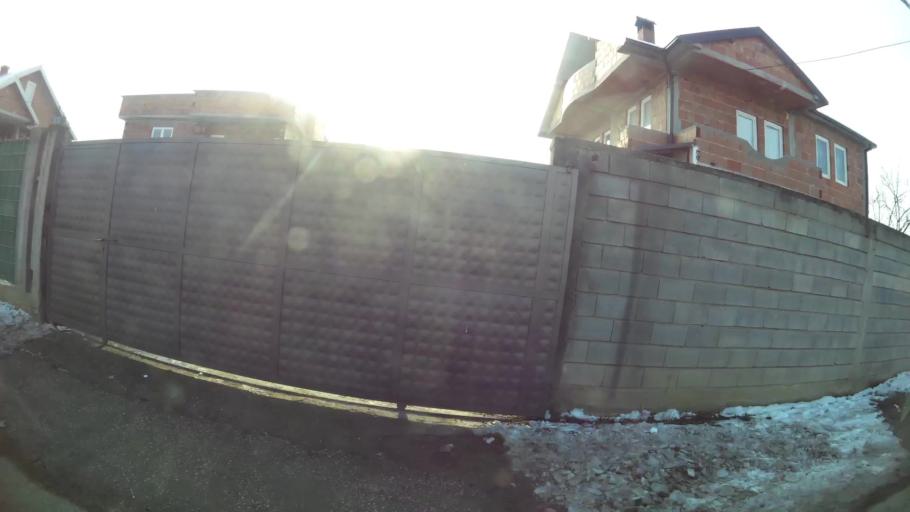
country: MK
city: Creshevo
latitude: 42.0218
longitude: 21.5013
